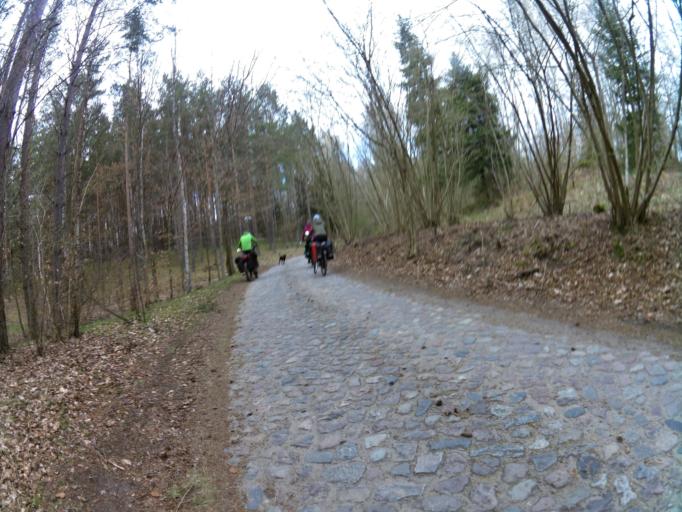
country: PL
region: West Pomeranian Voivodeship
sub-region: Powiat koszalinski
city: Bobolice
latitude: 53.8644
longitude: 16.6854
